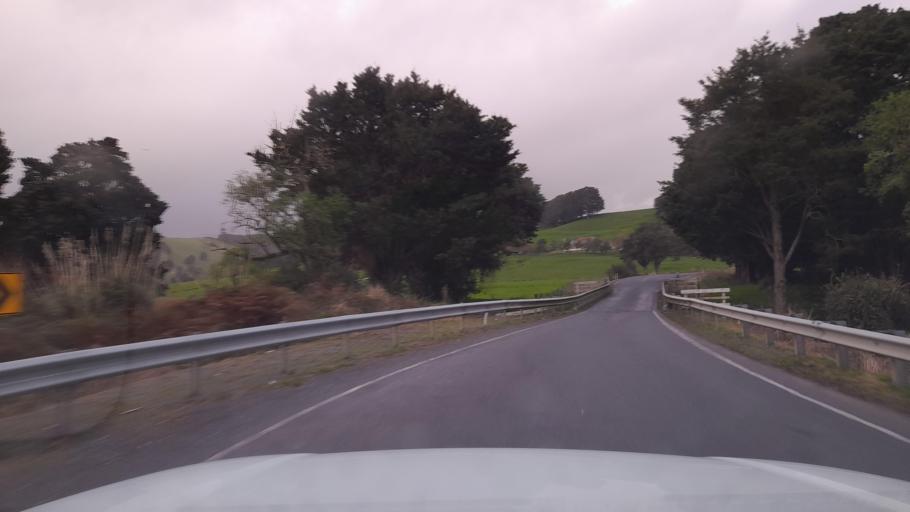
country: NZ
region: Northland
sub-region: Whangarei
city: Maungatapere
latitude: -35.6988
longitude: 174.1813
